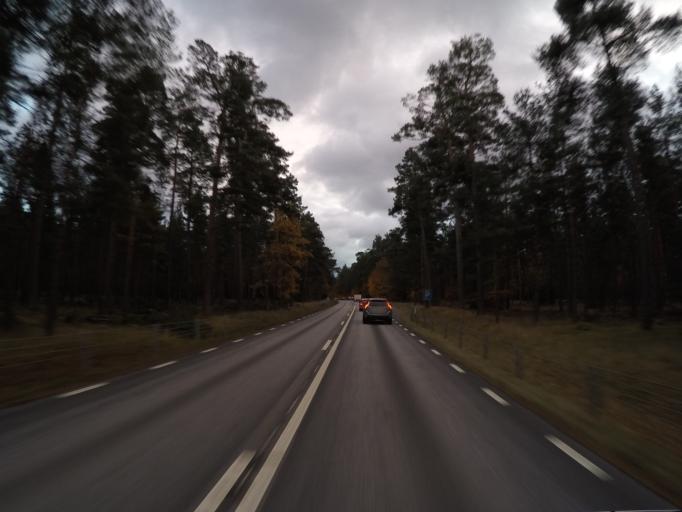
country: SE
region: Skane
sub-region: Kristianstads Kommun
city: Degeberga
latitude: 55.8685
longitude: 14.0890
